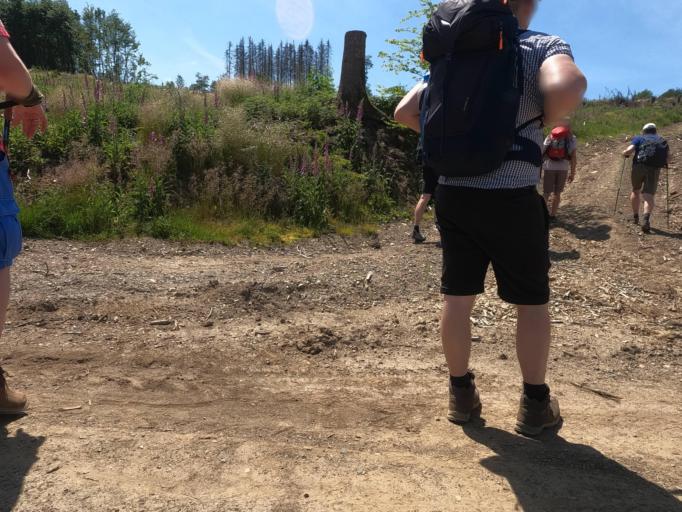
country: DE
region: Rheinland-Pfalz
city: Alpenrod
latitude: 50.6478
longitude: 7.8681
